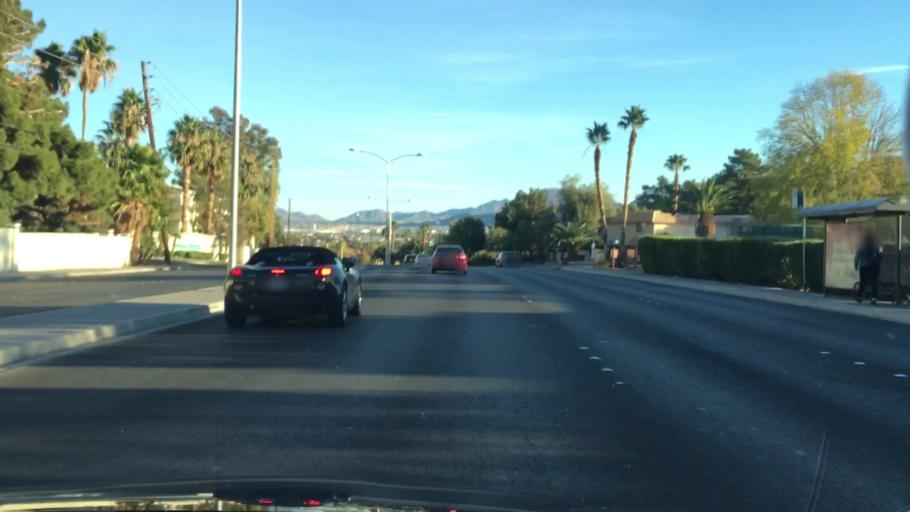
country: US
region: Nevada
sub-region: Clark County
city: Whitney
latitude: 36.0661
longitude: -115.0663
